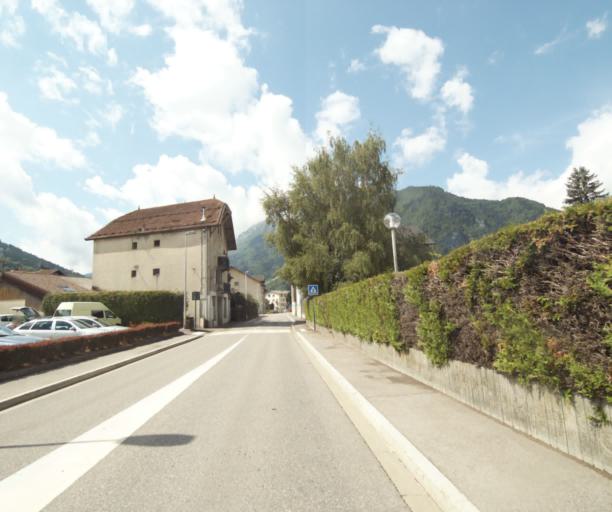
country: FR
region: Rhone-Alpes
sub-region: Departement de la Haute-Savoie
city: Thones
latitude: 45.8848
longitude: 6.3280
